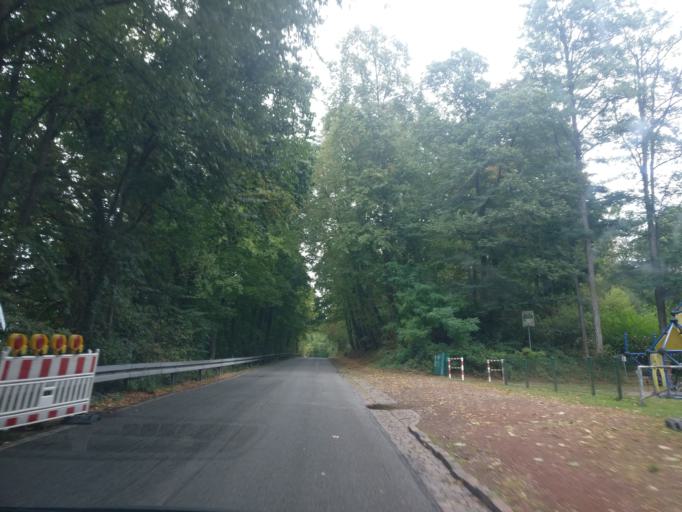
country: DE
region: Saarland
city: Homburg
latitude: 49.3219
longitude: 7.3479
